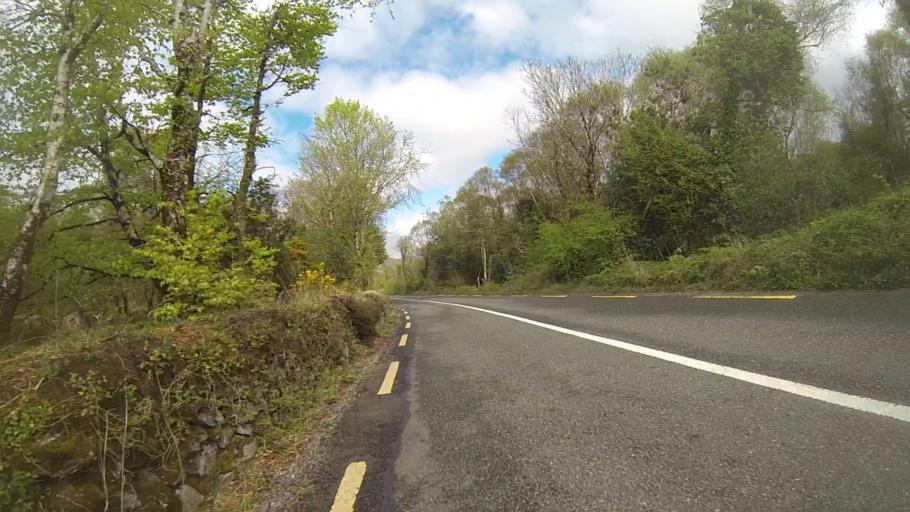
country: IE
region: Munster
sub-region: Ciarrai
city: Kenmare
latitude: 51.8248
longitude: -9.8548
